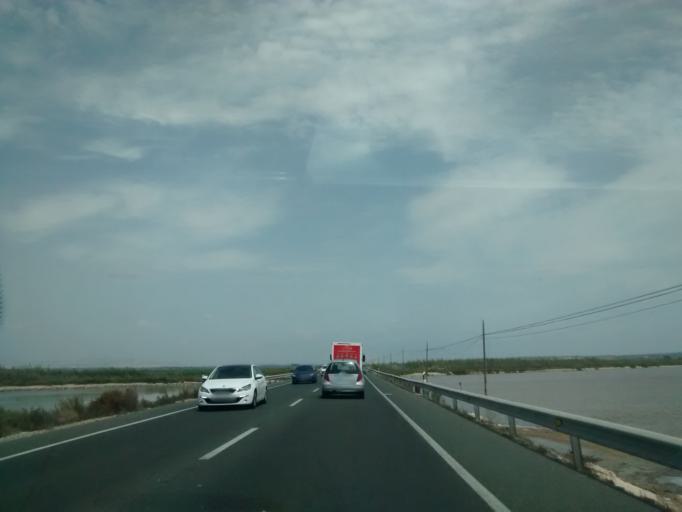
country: ES
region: Valencia
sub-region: Provincia de Alicante
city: Santa Pola
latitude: 38.1770
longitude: -0.6206
